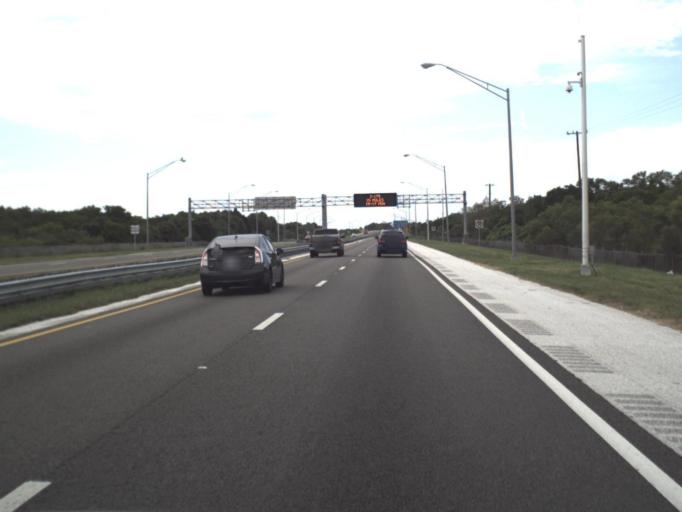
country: US
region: Florida
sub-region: Manatee County
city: Memphis
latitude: 27.5836
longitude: -82.6018
